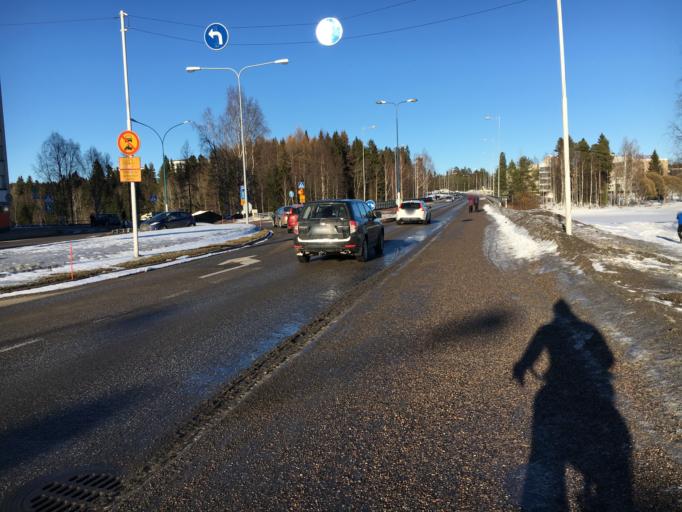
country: FI
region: Kainuu
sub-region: Kajaani
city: Kajaani
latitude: 64.2250
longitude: 27.7352
